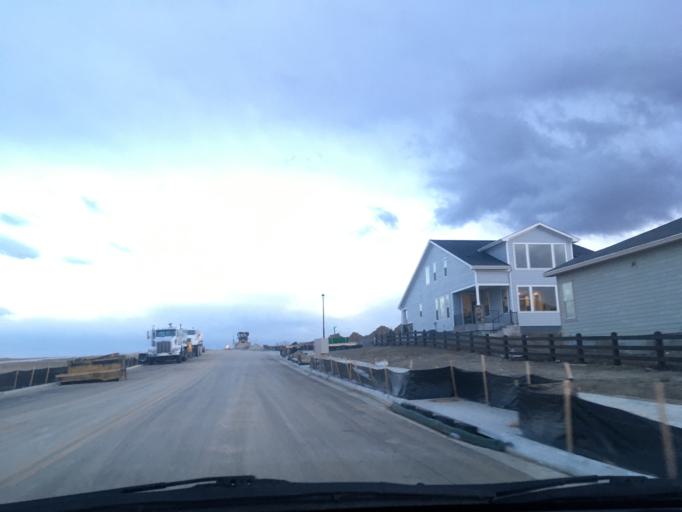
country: US
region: Colorado
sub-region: Adams County
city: Todd Creek
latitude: 39.9569
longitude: -104.9132
